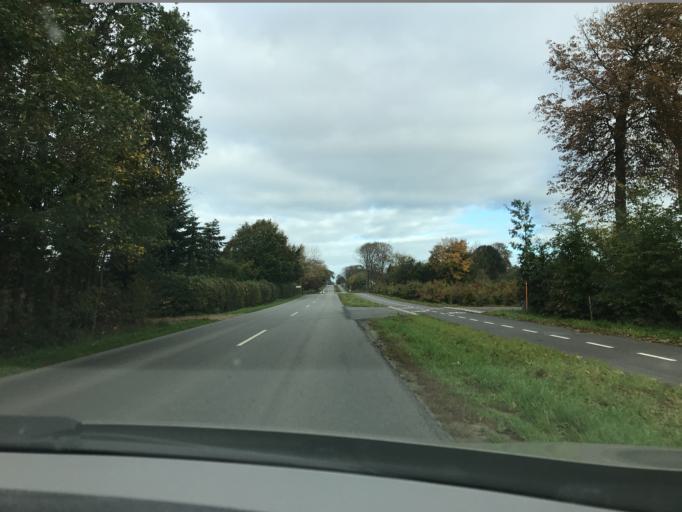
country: DK
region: South Denmark
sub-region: Kolding Kommune
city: Kolding
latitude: 55.5491
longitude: 9.4130
